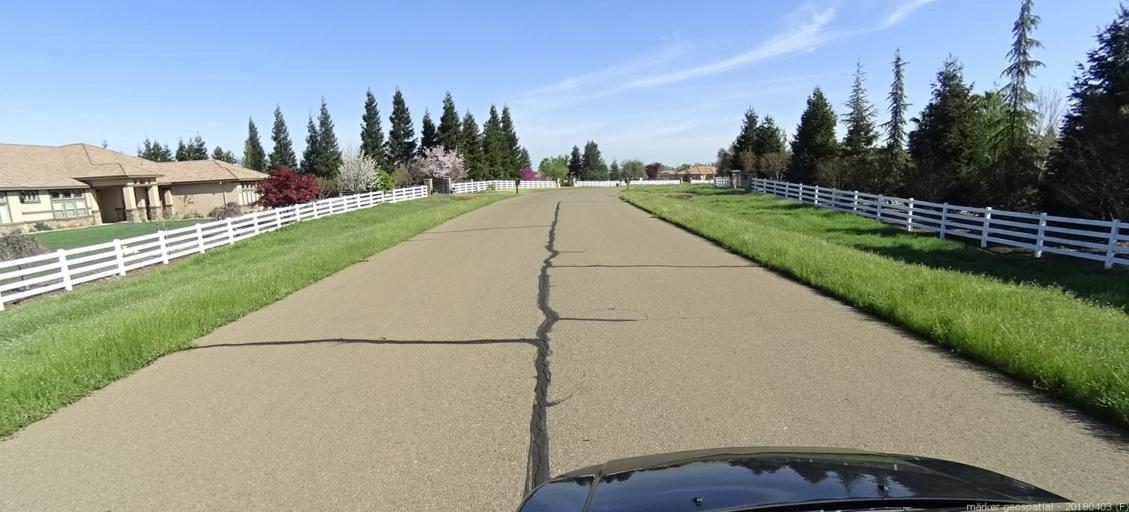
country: US
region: California
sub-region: Sacramento County
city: Wilton
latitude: 38.4140
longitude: -121.1919
